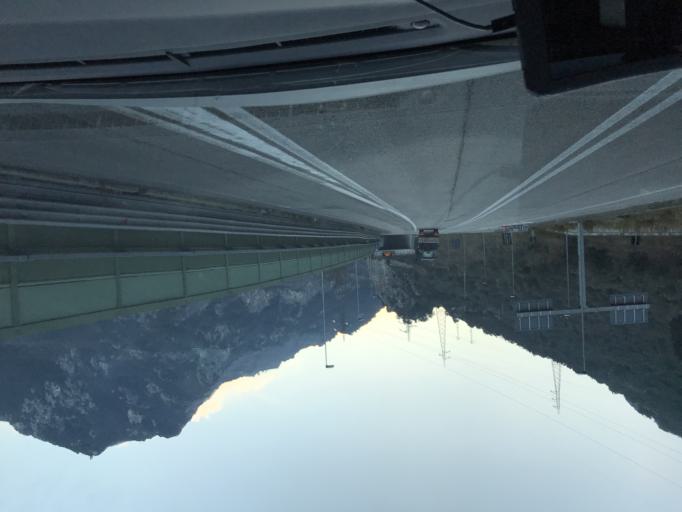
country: IT
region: Umbria
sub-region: Provincia di Terni
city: Terni
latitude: 42.5558
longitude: 12.6952
